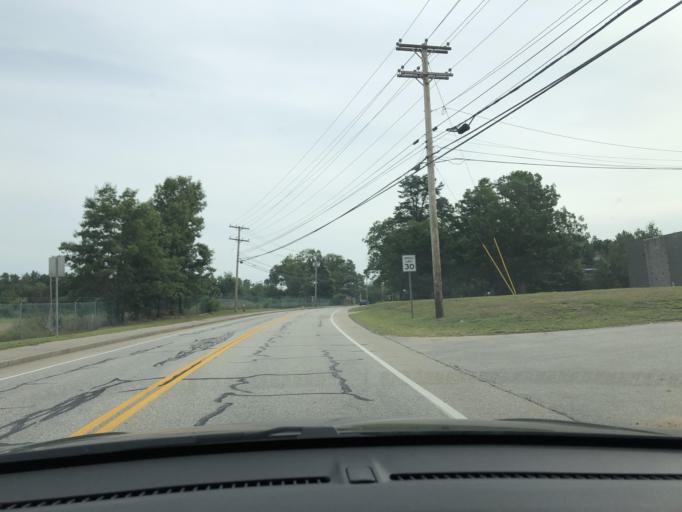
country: US
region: New Hampshire
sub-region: Merrimack County
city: Concord
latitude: 43.2010
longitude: -71.5164
